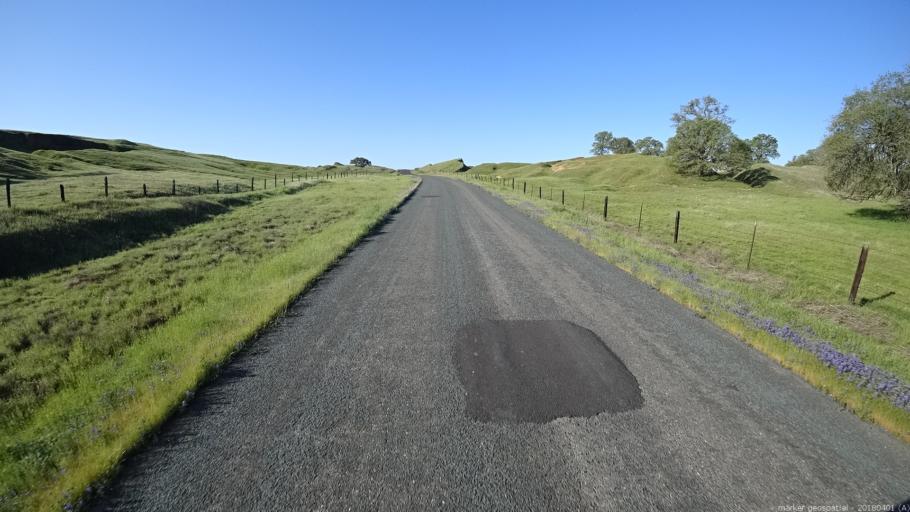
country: US
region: California
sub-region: Sacramento County
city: Rancho Murieta
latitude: 38.4896
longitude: -121.0507
